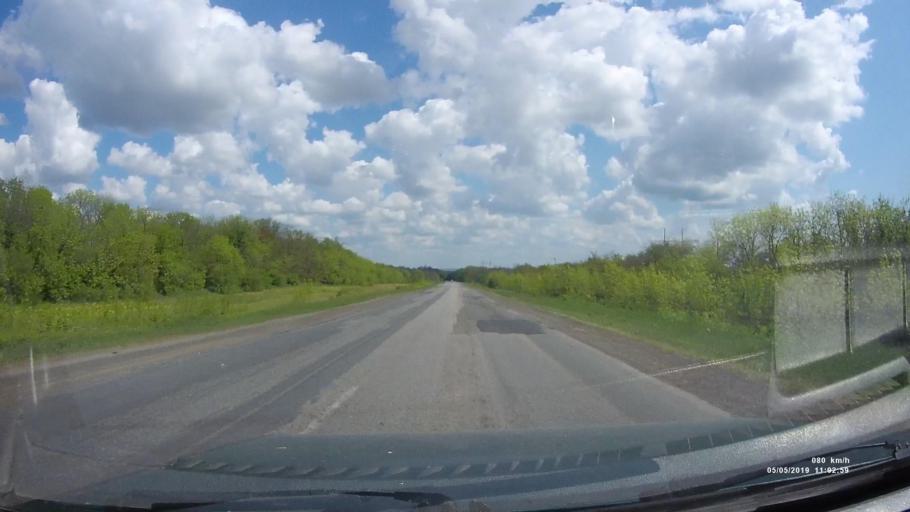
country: RU
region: Rostov
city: Ust'-Donetskiy
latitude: 47.6884
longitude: 40.9149
